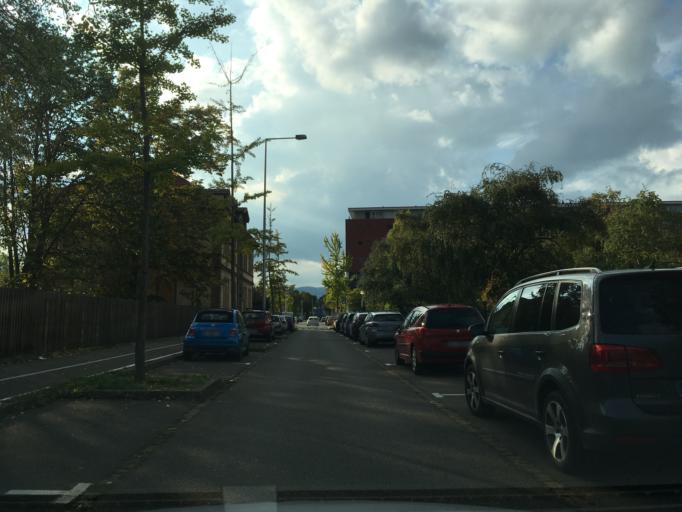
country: FR
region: Alsace
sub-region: Departement du Haut-Rhin
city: Colmar
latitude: 48.0830
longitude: 7.3440
